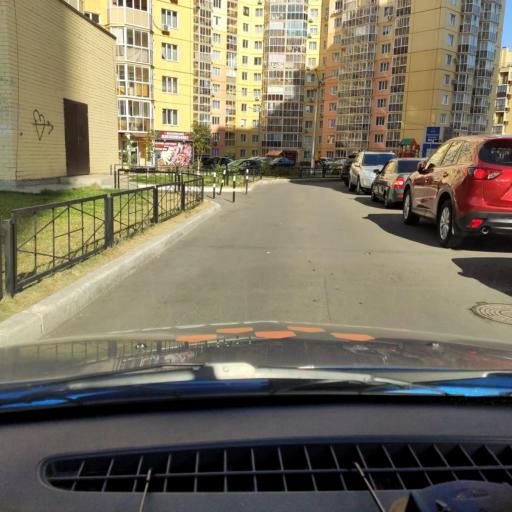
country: RU
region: Voronezj
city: Voronezh
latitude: 51.7026
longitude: 39.2002
